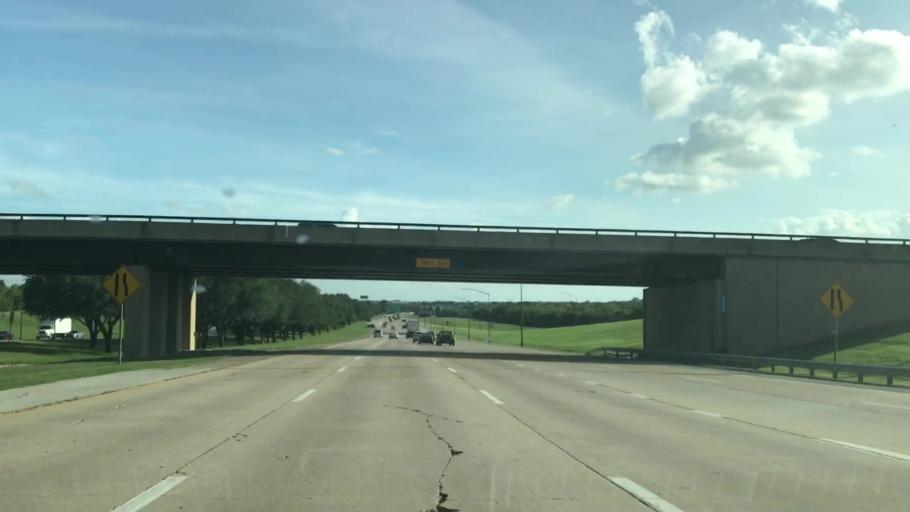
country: US
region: Texas
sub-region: Tarrant County
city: Euless
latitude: 32.8534
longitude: -97.0410
